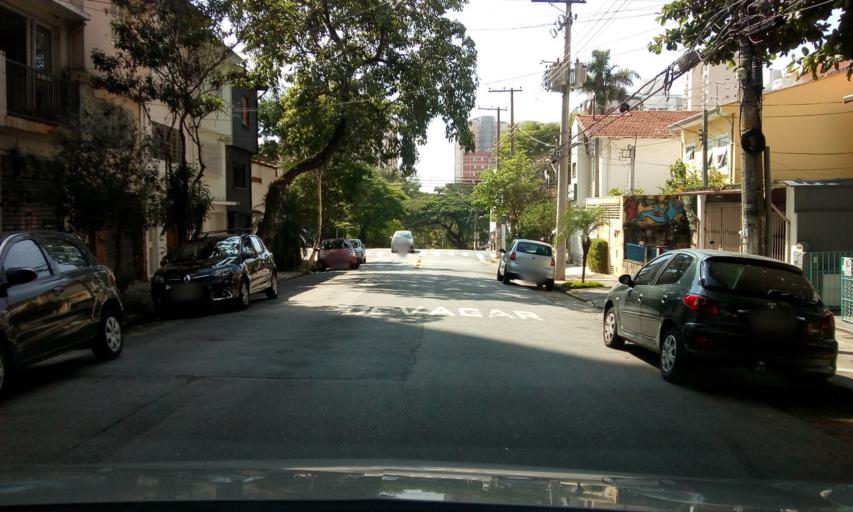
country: BR
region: Sao Paulo
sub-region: Sao Paulo
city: Sao Paulo
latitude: -23.5380
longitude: -46.6819
